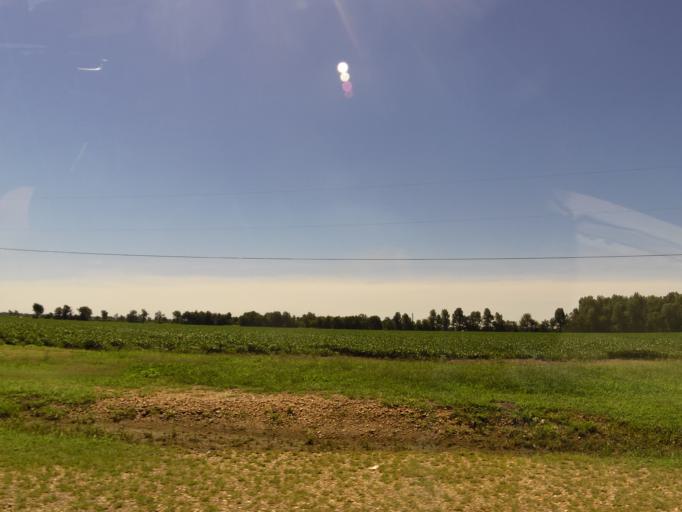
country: US
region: Missouri
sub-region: New Madrid County
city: Lilbourn
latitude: 36.5656
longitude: -89.6079
